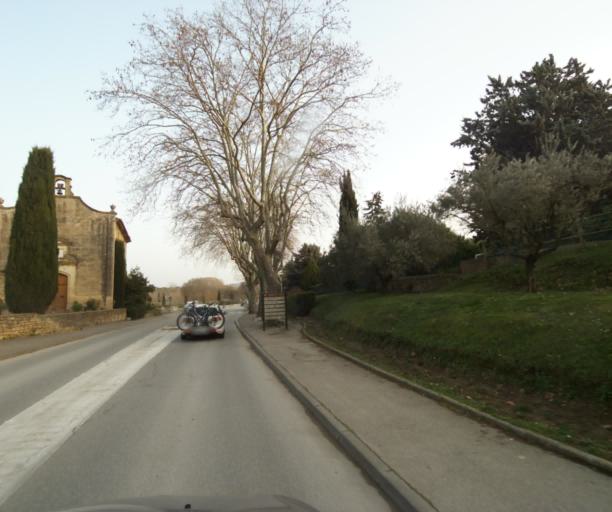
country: FR
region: Provence-Alpes-Cote d'Azur
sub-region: Departement des Bouches-du-Rhone
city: Rognes
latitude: 43.6616
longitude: 5.3516
